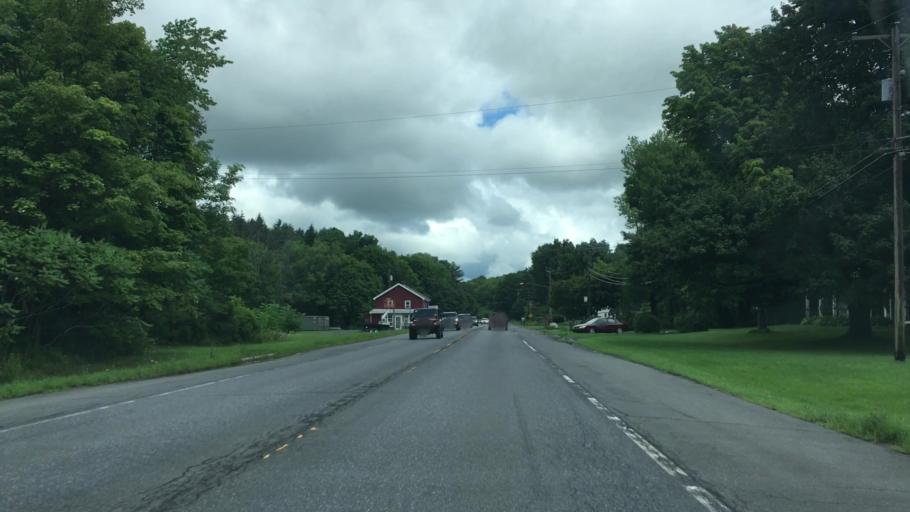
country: US
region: New York
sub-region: Rensselaer County
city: Poestenkill
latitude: 42.7878
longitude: -73.5733
